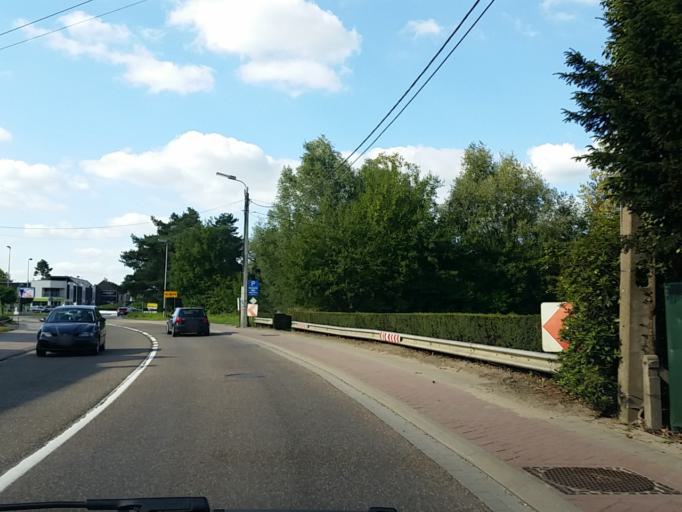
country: BE
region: Flanders
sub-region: Provincie Vlaams-Brabant
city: Holsbeek
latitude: 50.9385
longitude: 4.7384
